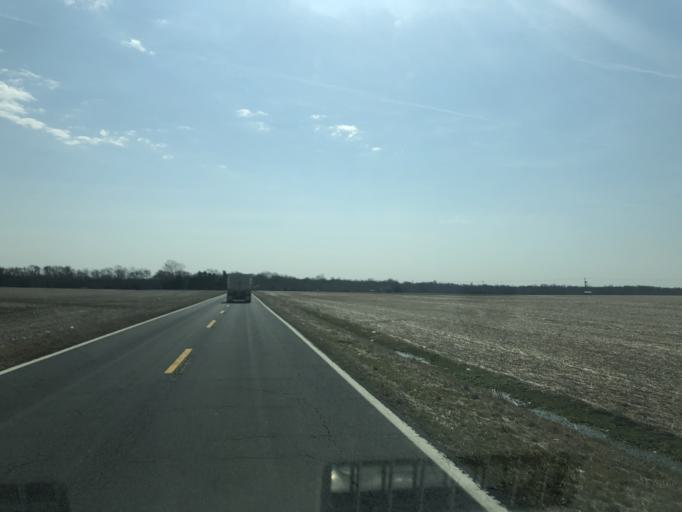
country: US
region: Maryland
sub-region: Caroline County
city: Ridgely
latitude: 39.0329
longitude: -75.9025
